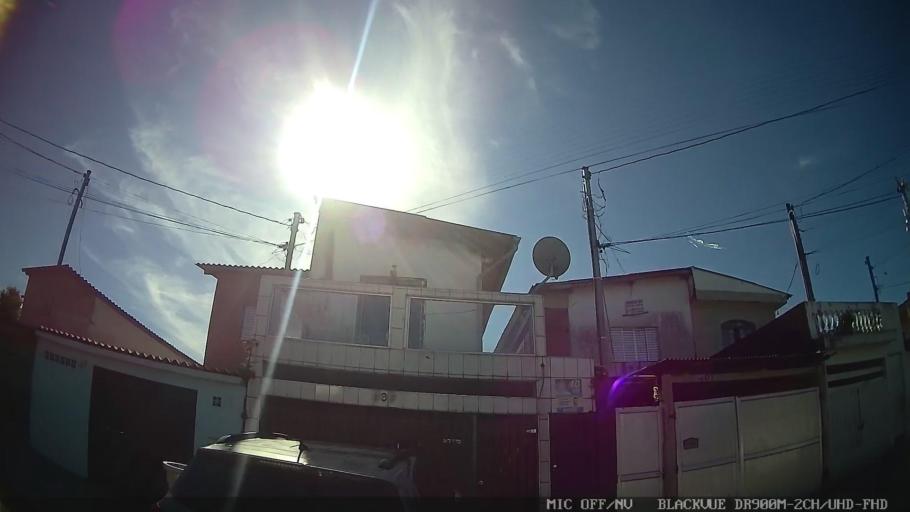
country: BR
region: Sao Paulo
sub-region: Santos
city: Santos
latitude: -23.9379
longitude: -46.2840
